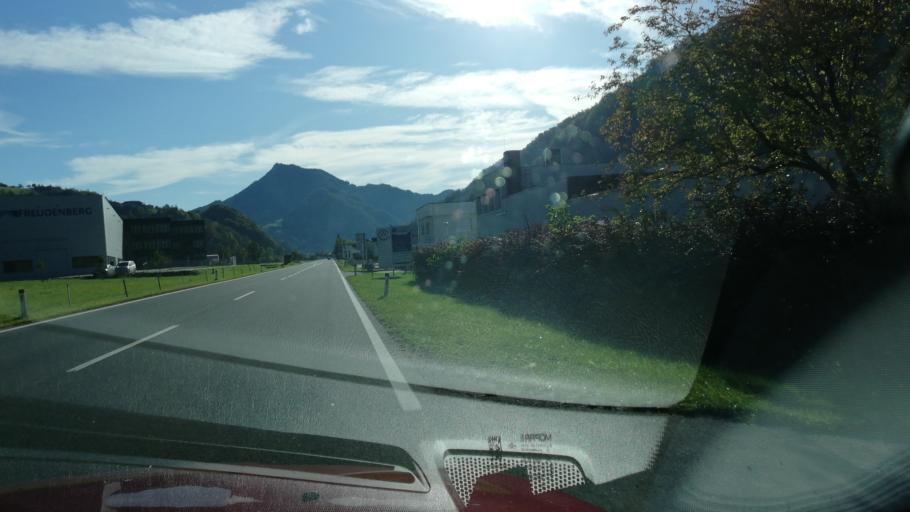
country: AT
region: Upper Austria
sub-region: Politischer Bezirk Steyr-Land
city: Losenstein
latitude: 47.9323
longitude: 14.4035
